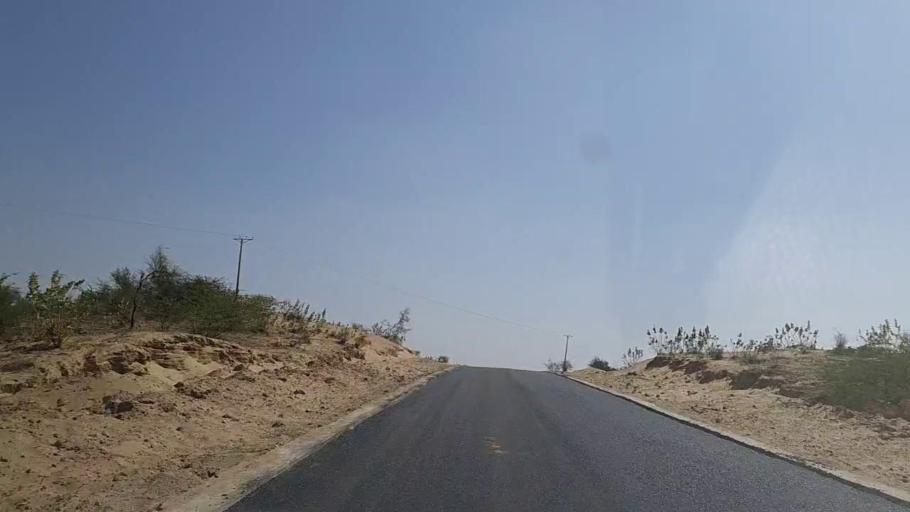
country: PK
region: Sindh
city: Diplo
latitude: 24.4796
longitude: 69.5286
